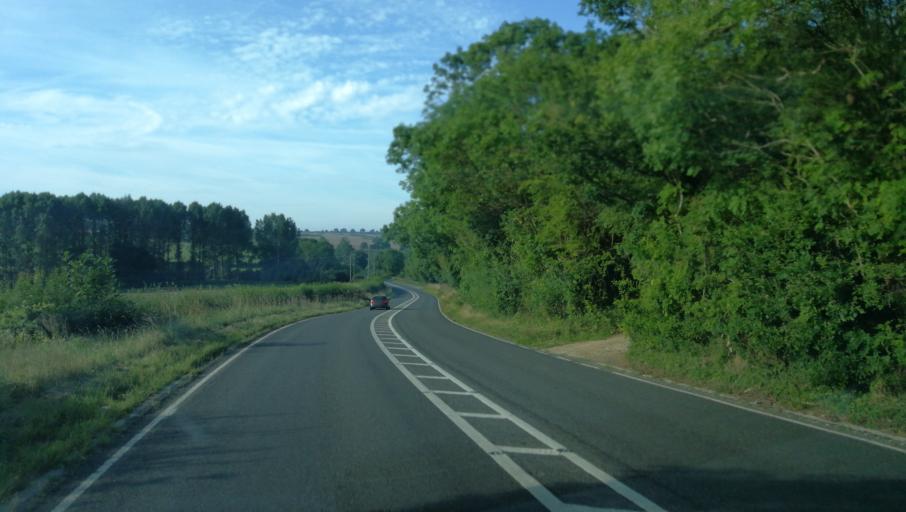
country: GB
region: England
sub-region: Oxfordshire
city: Deddington
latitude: 51.9711
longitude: -1.3188
